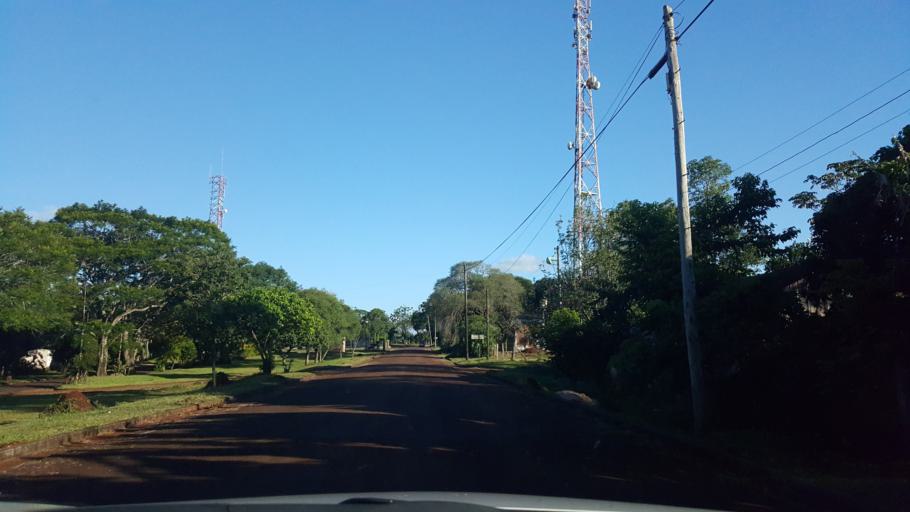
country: AR
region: Misiones
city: Gobernador Roca
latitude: -27.1277
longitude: -55.5131
